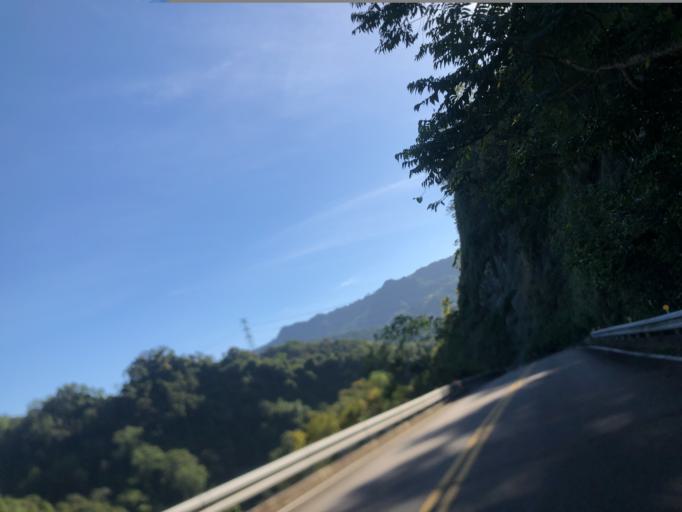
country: TW
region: Taiwan
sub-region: Miaoli
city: Miaoli
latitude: 24.5810
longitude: 120.9327
